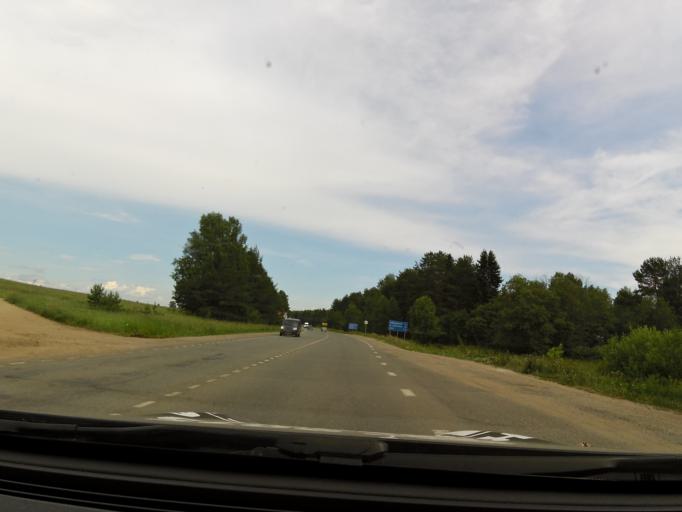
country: RU
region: Kirov
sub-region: Kirovo-Chepetskiy Rayon
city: Kirov
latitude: 58.6235
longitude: 49.7841
